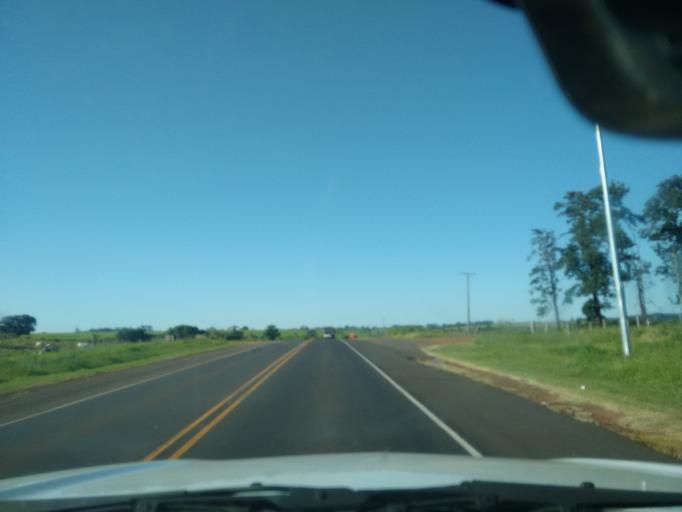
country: PY
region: Canindeyu
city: Salto del Guaira
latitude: -23.9737
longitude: -54.3309
